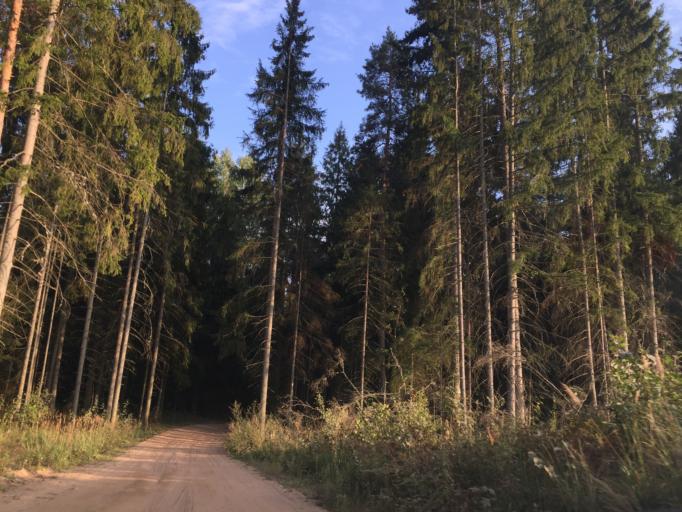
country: LV
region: Baldone
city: Baldone
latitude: 56.7611
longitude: 24.4098
